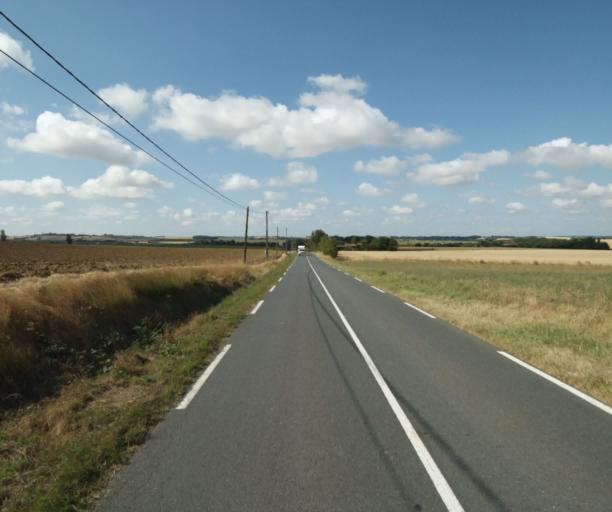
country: FR
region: Midi-Pyrenees
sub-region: Departement de la Haute-Garonne
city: Auriac-sur-Vendinelle
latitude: 43.4539
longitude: 1.8169
